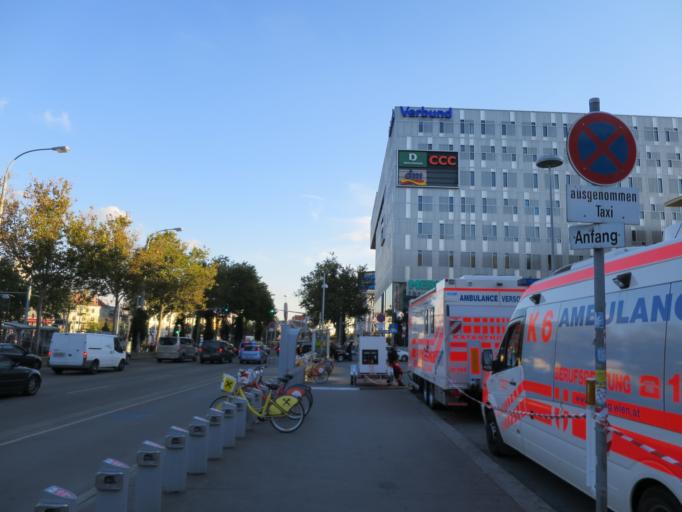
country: AT
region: Vienna
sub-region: Wien Stadt
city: Vienna
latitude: 48.1971
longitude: 16.3385
